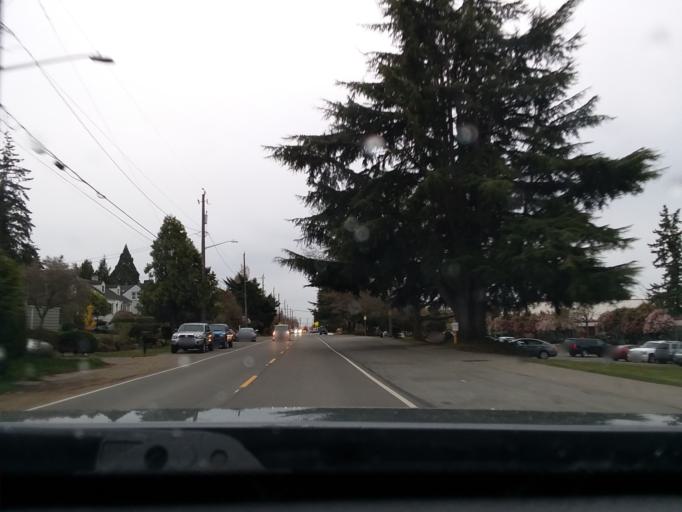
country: US
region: Washington
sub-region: King County
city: Shoreline
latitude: 47.6978
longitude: -122.3768
